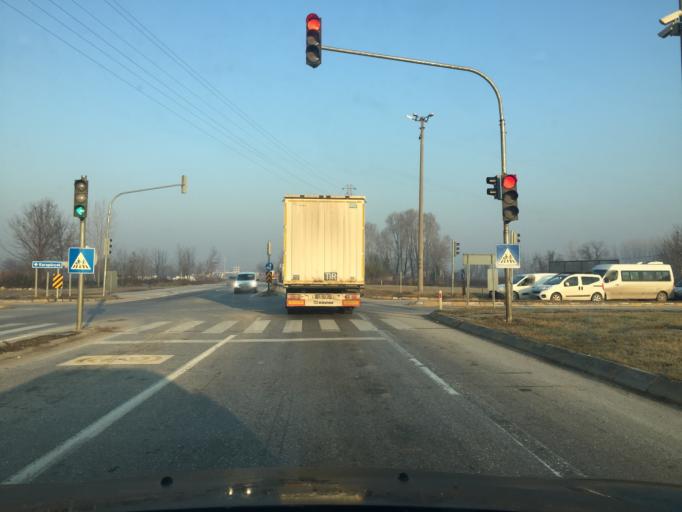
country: TR
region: Sakarya
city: Akyazi
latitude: 40.6740
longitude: 30.5861
